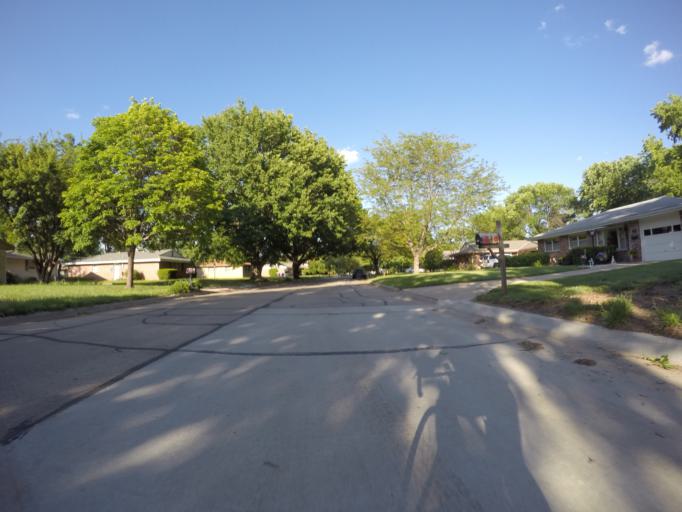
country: US
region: Kansas
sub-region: Riley County
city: Manhattan
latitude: 39.2027
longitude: -96.6044
